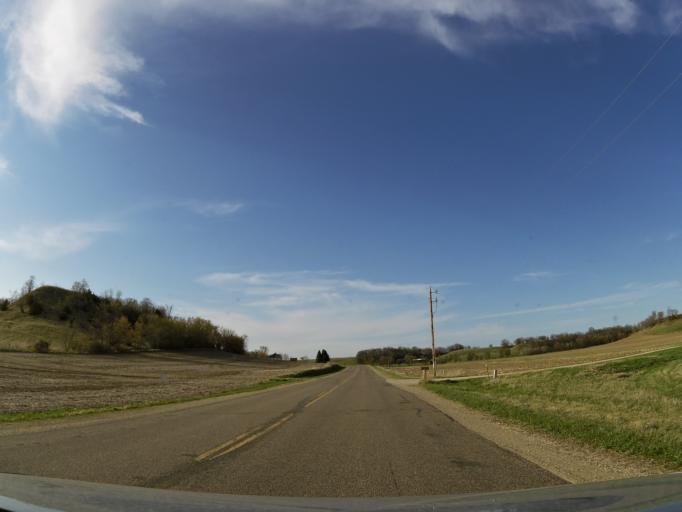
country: US
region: Wisconsin
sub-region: Pierce County
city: River Falls
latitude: 44.7768
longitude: -92.6398
